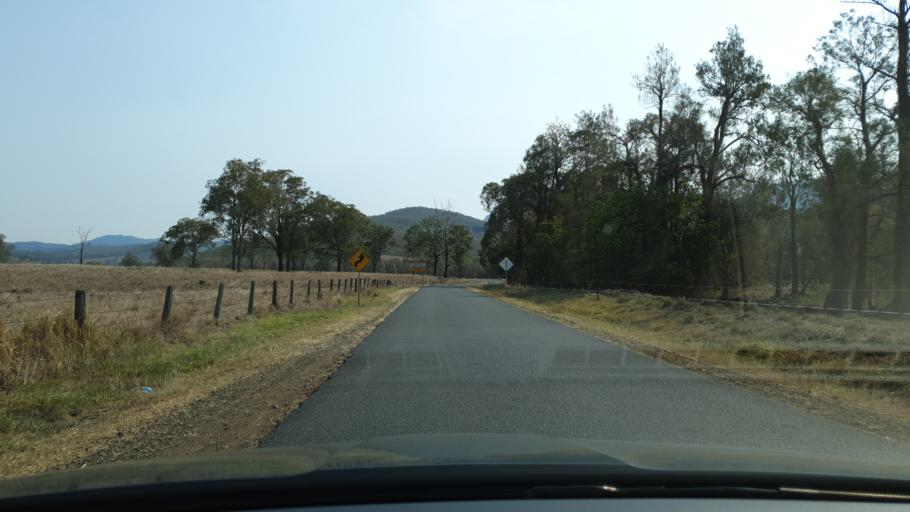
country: AU
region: Queensland
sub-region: Southern Downs
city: Warwick
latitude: -28.1833
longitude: 152.5459
